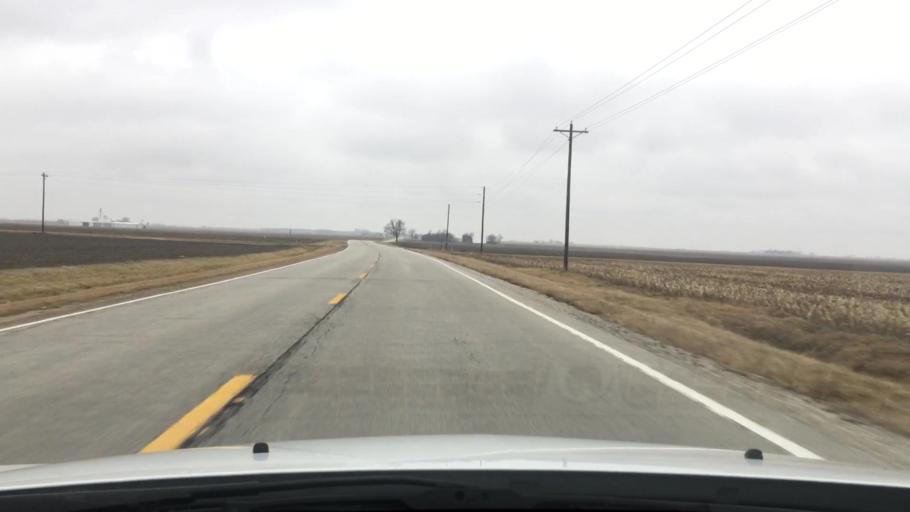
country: US
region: Illinois
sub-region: Iroquois County
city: Clifton
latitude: 40.8869
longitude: -87.8829
